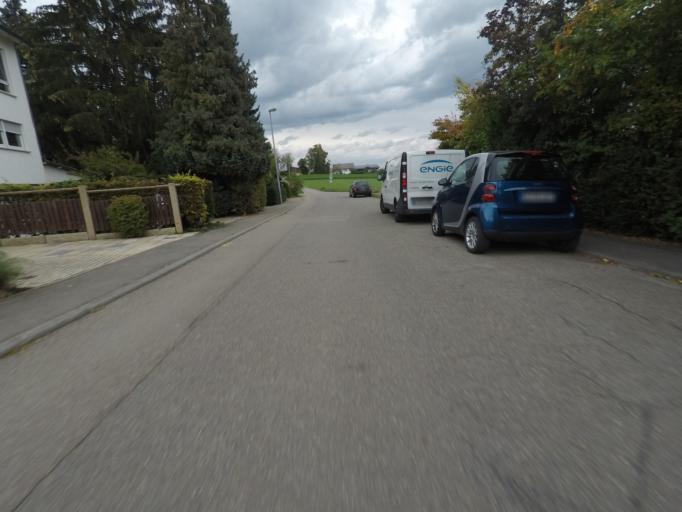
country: DE
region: Baden-Wuerttemberg
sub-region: Regierungsbezirk Stuttgart
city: Filderstadt
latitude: 48.6605
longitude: 9.1933
